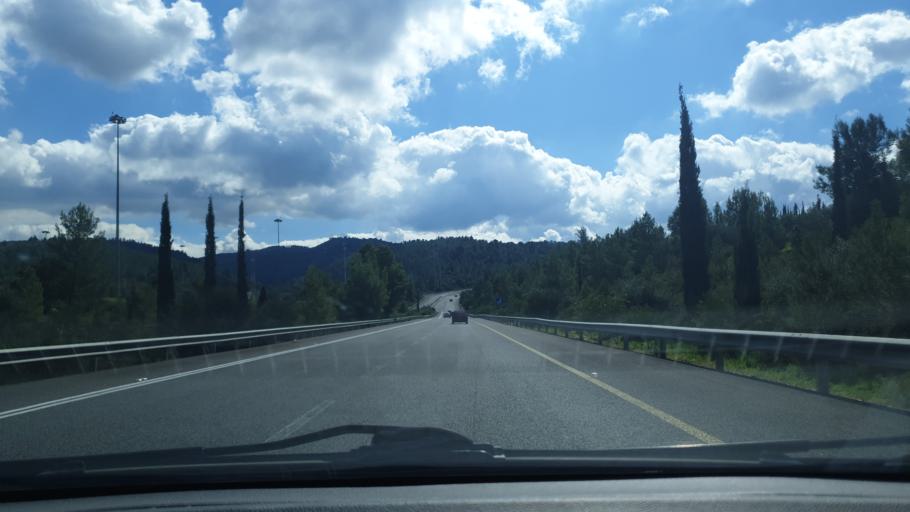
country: IL
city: Mevo horon
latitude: 31.8194
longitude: 35.0194
